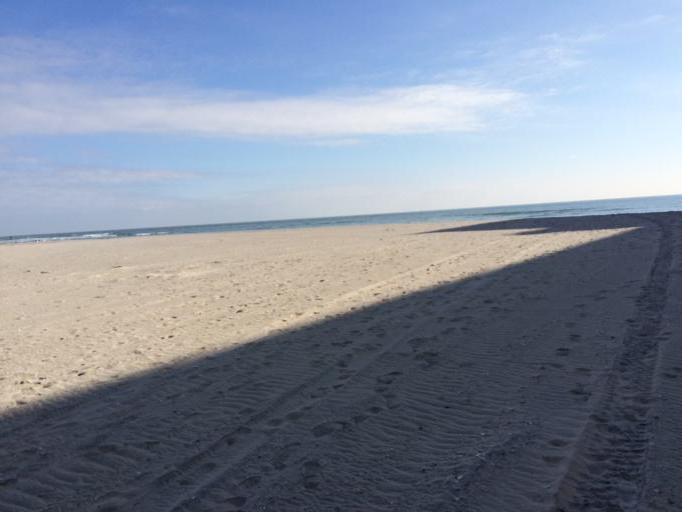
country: US
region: New Jersey
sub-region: Atlantic County
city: Atlantic City
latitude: 39.3542
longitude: -74.4338
